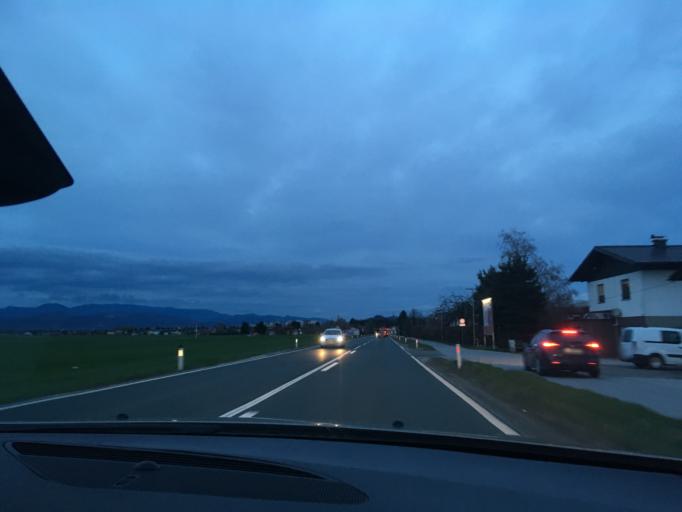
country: SI
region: Trzin
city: Trzin
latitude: 46.1349
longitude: 14.5723
